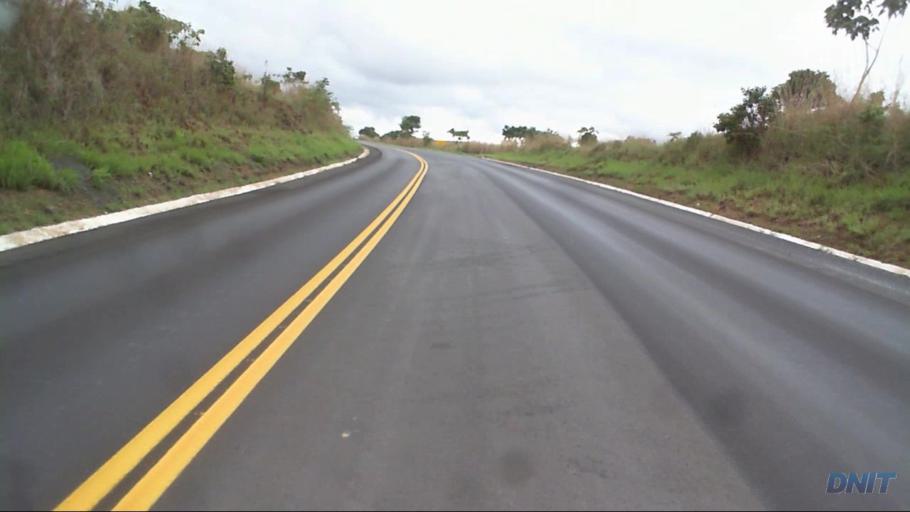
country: BR
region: Goias
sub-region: Padre Bernardo
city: Padre Bernardo
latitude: -15.2210
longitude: -48.5254
